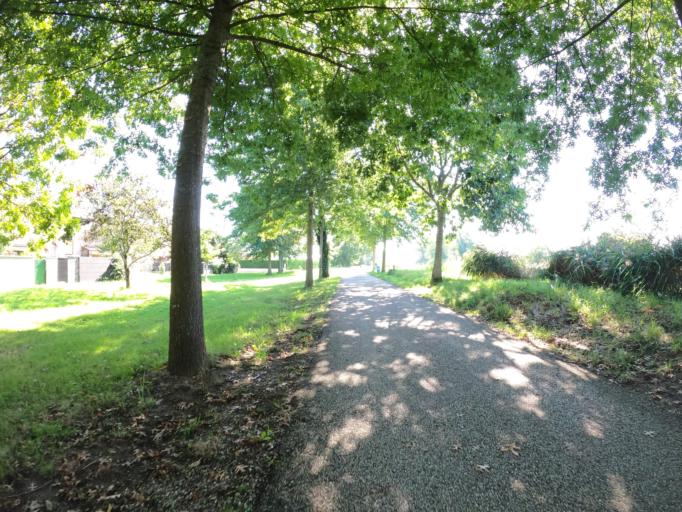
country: FR
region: Aquitaine
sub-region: Departement du Lot-et-Garonne
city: Bon-Encontre
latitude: 44.1843
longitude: 0.6567
